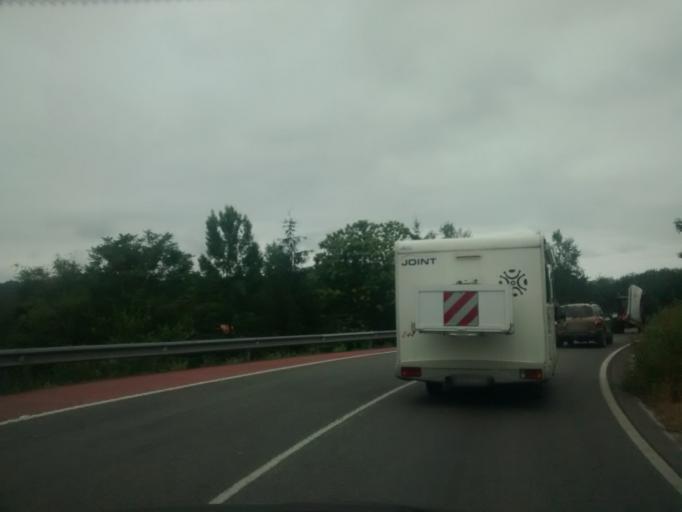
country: ES
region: Cantabria
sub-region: Provincia de Cantabria
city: Luzmela
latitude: 43.3119
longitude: -4.1963
